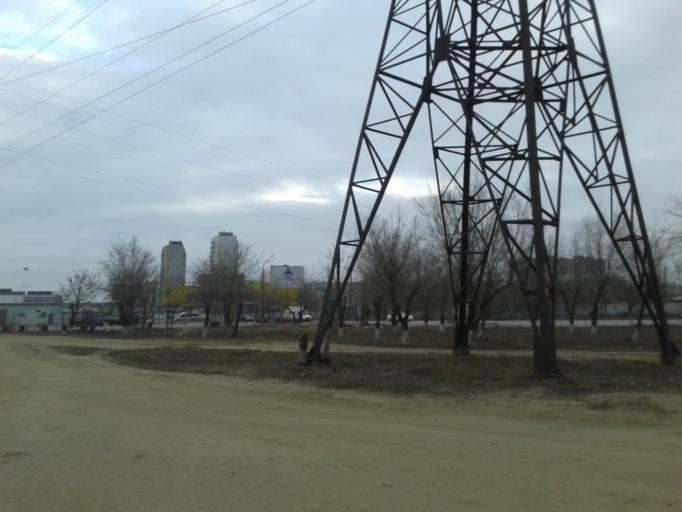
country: RU
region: Volgograd
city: Gorodishche
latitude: 48.7658
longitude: 44.4733
